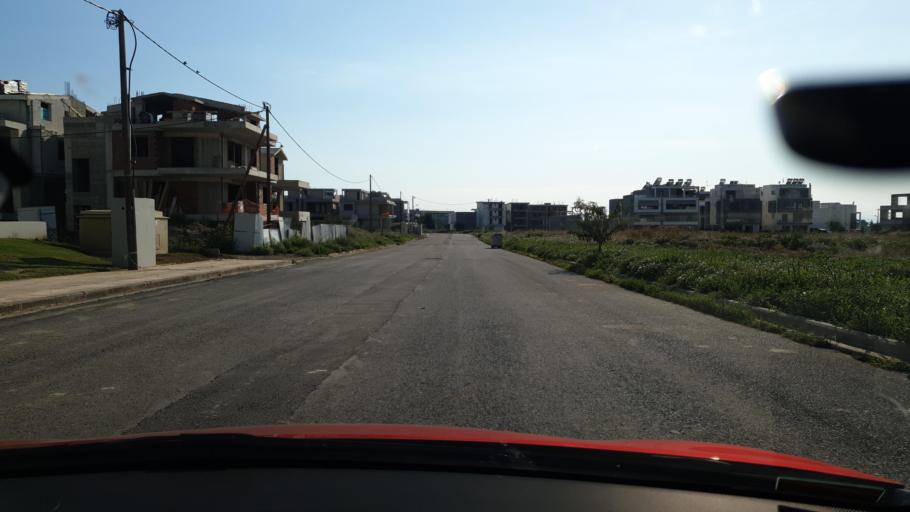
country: GR
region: Central Macedonia
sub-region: Nomos Thessalonikis
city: Thermi
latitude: 40.5429
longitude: 23.0146
